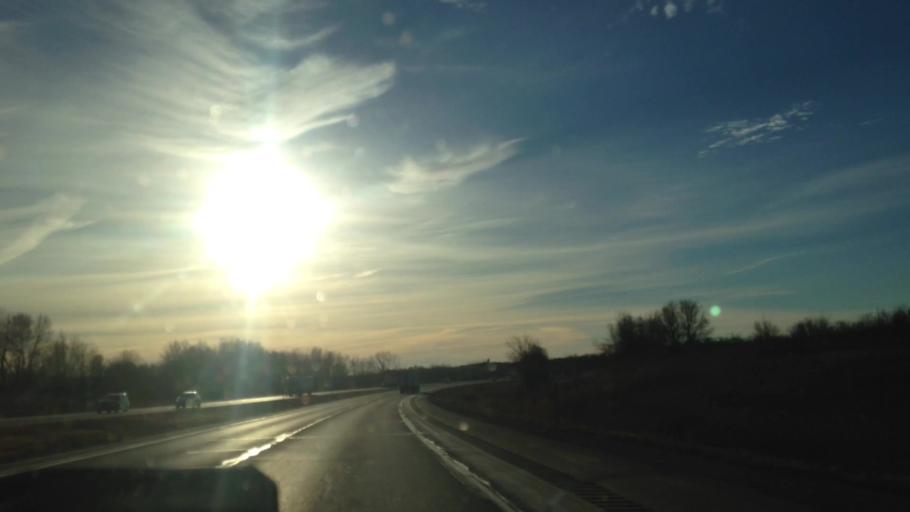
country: US
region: Wisconsin
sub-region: Dodge County
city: Theresa
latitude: 43.5112
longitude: -88.3719
